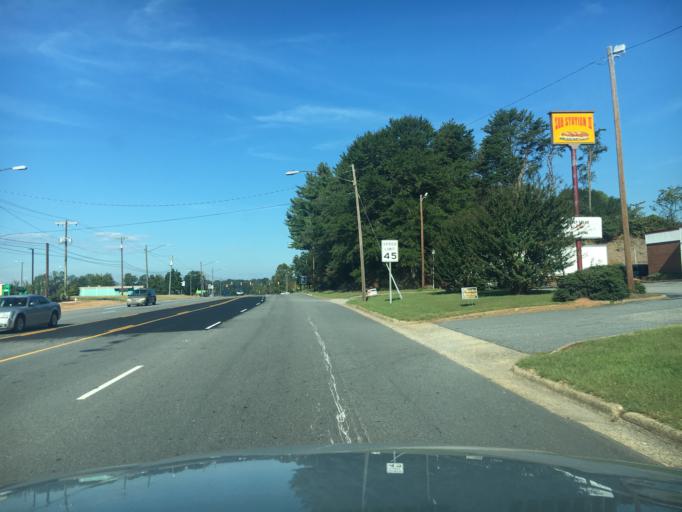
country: US
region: North Carolina
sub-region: Catawba County
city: Hickory
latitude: 35.7191
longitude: -81.3441
